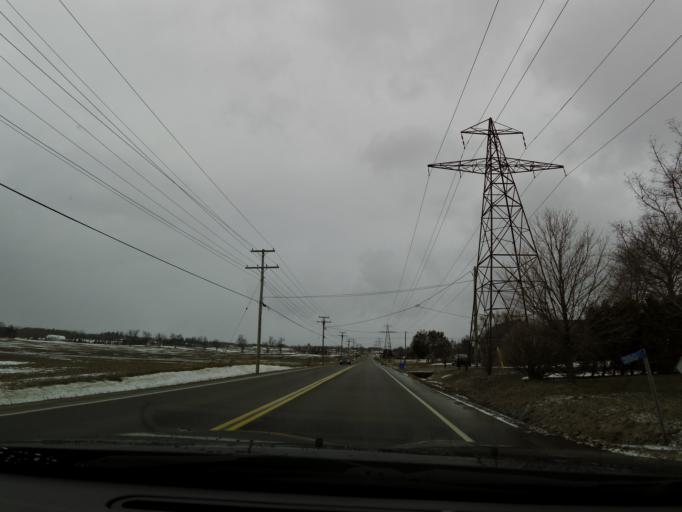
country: CA
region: Ontario
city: Ancaster
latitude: 43.2929
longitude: -79.9474
